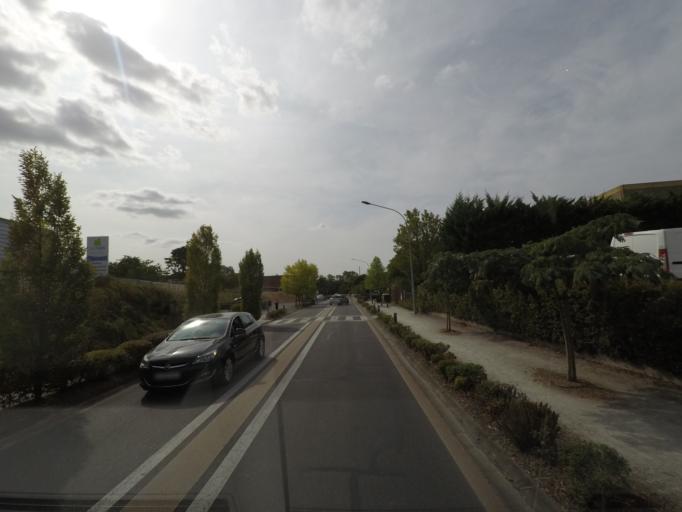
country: FR
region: Poitou-Charentes
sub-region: Departement de la Charente
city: Ruffec
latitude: 46.0311
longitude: 0.2031
